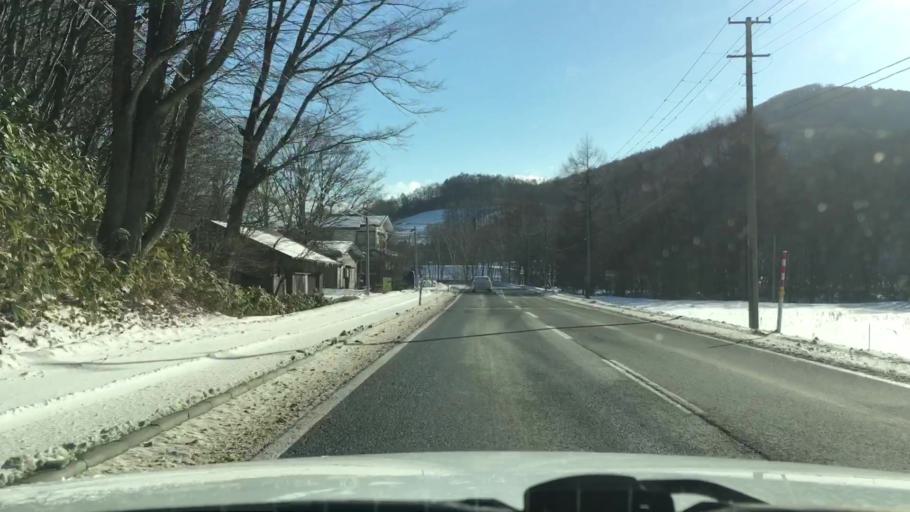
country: JP
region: Iwate
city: Morioka-shi
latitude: 39.6432
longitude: 141.3758
